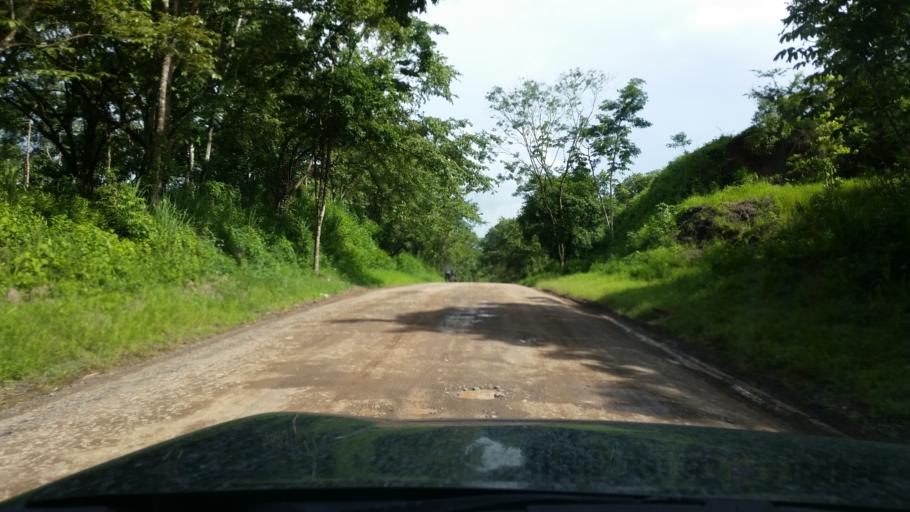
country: NI
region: Atlantico Norte (RAAN)
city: Siuna
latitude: 13.6674
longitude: -84.7924
